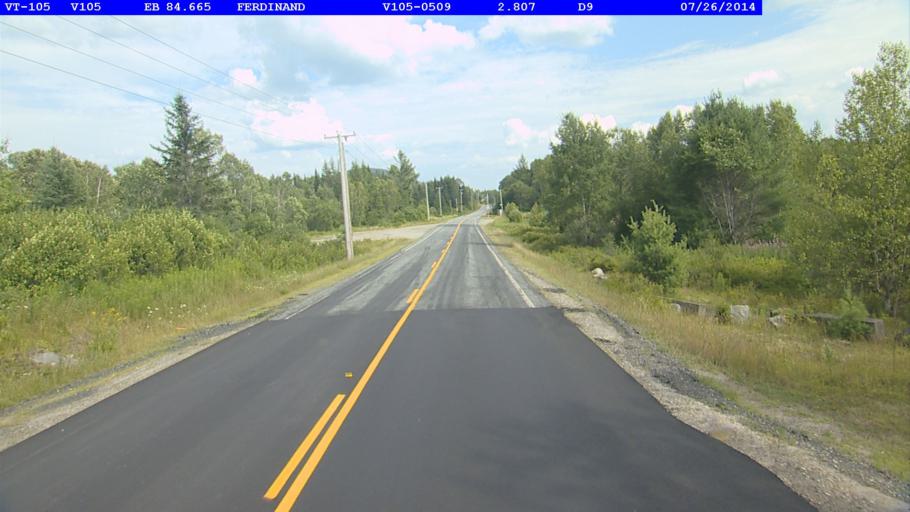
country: US
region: New Hampshire
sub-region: Coos County
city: Stratford
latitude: 44.7768
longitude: -71.7496
